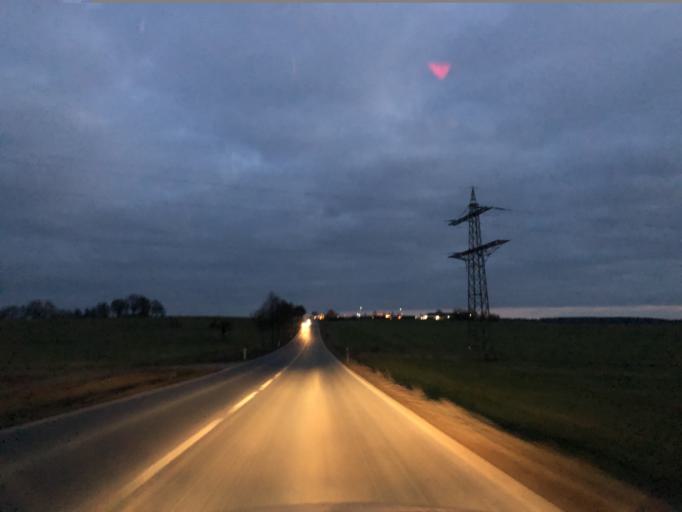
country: DE
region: Rheinland-Pfalz
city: Singhofen
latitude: 50.2858
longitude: 7.8284
